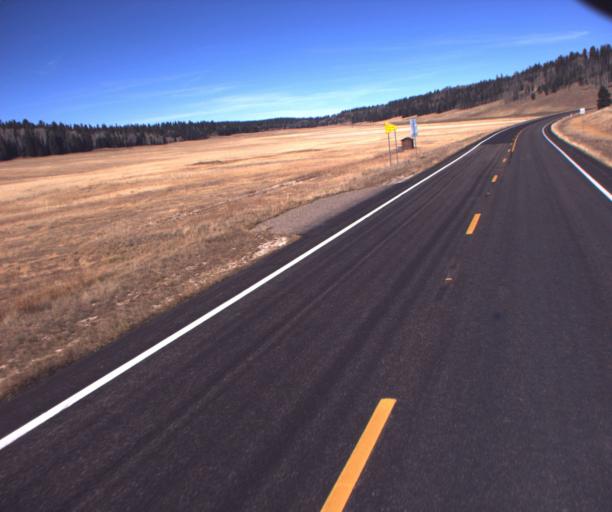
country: US
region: Arizona
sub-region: Coconino County
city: Grand Canyon
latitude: 36.4155
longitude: -112.1308
